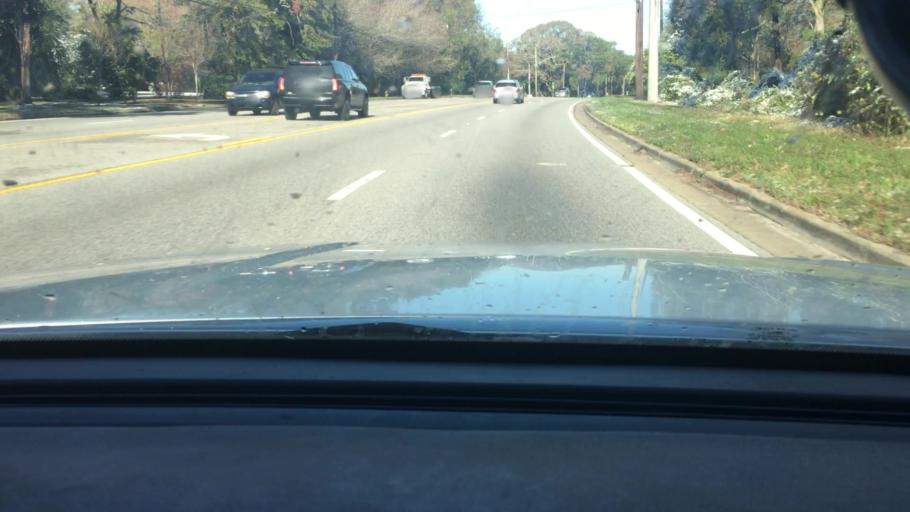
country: US
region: Alabama
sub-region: Mobile County
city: Prichard
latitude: 30.7313
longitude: -88.1743
